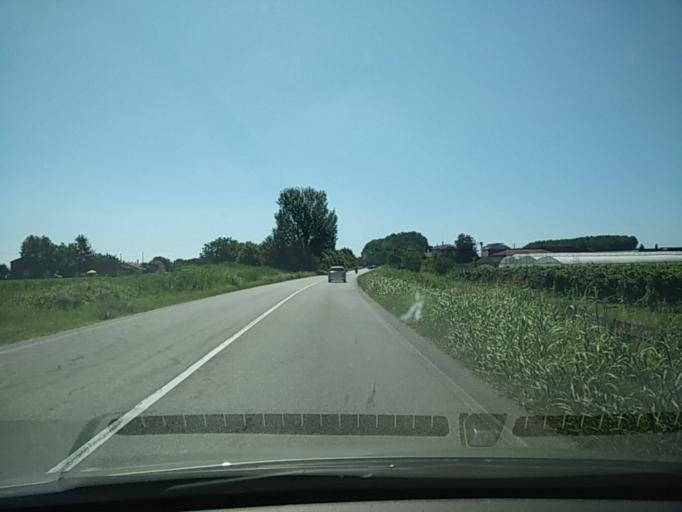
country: IT
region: Veneto
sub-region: Provincia di Venezia
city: San Giorgio di Livenza
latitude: 45.6312
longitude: 12.7766
